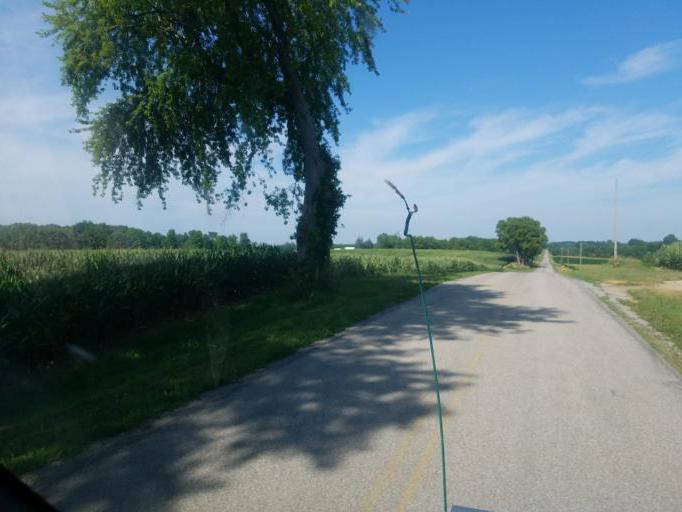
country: US
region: Ohio
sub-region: Hardin County
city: Kenton
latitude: 40.5535
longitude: -83.6584
